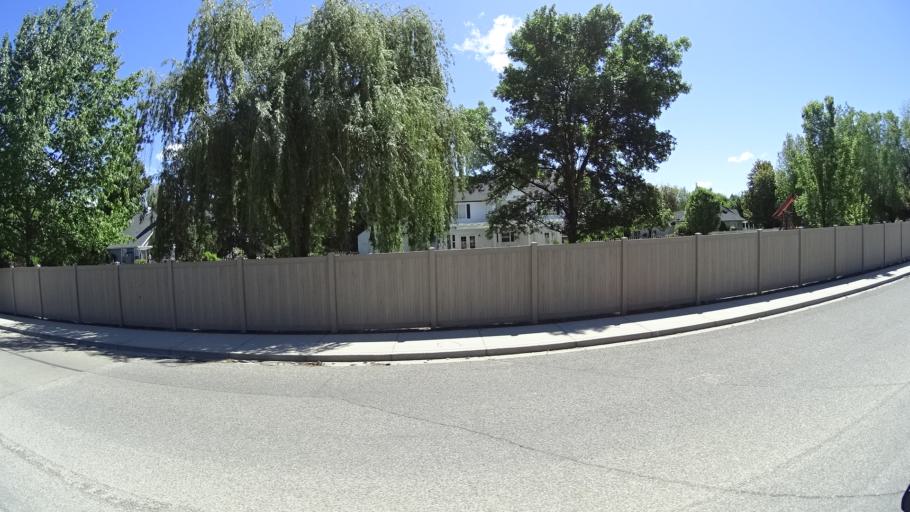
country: US
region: Idaho
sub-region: Ada County
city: Eagle
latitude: 43.6654
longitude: -116.3745
